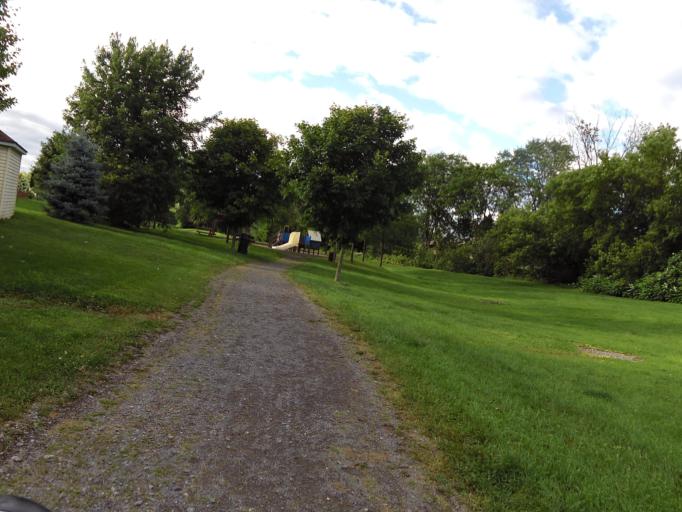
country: CA
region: Ontario
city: Bells Corners
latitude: 45.3286
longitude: -75.9134
